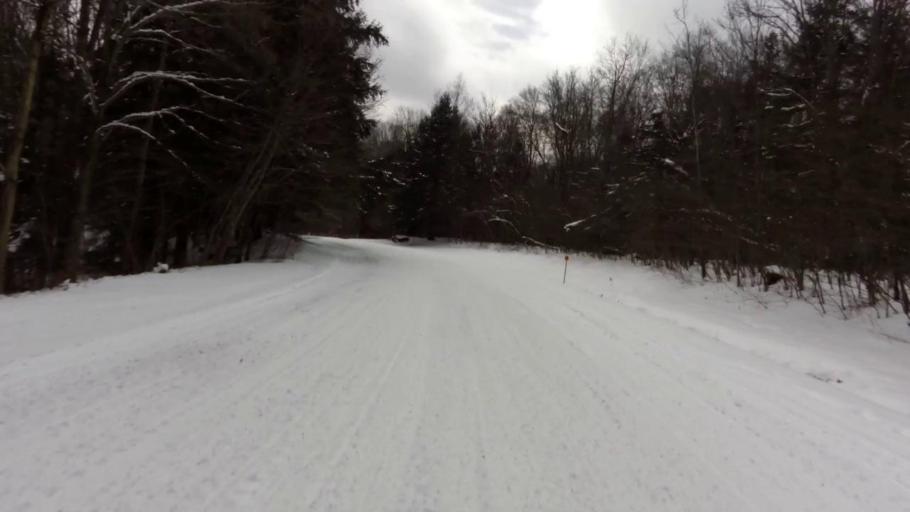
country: US
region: New York
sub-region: Cattaraugus County
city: Salamanca
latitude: 42.0192
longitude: -78.8220
